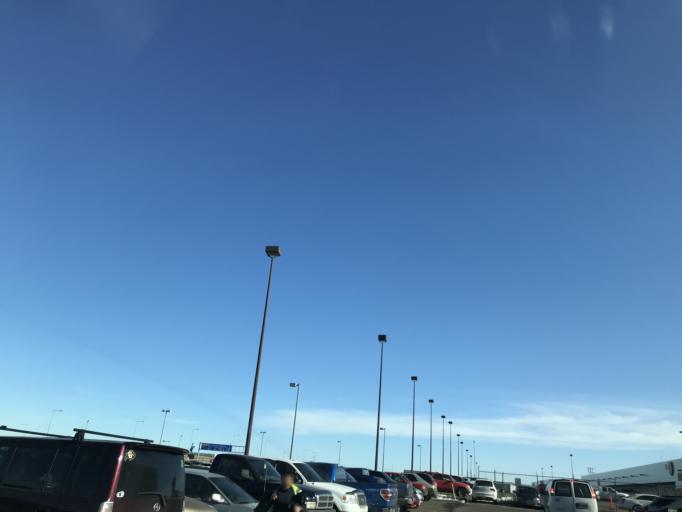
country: US
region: Colorado
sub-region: Weld County
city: Lochbuie
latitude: 39.8321
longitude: -104.6811
